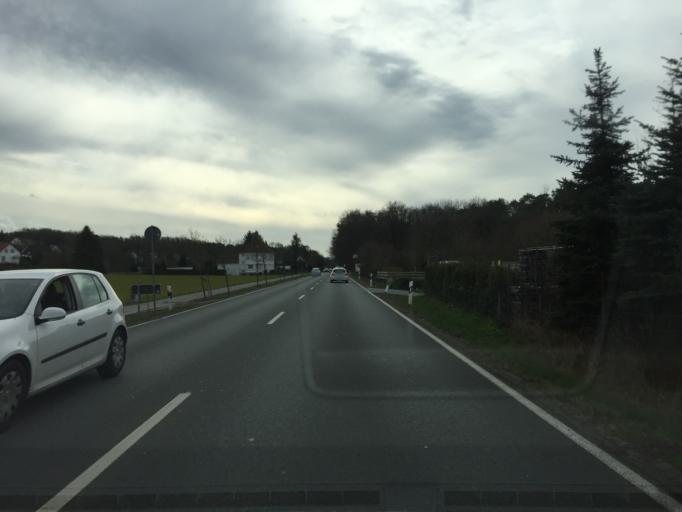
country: DE
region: North Rhine-Westphalia
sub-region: Regierungsbezirk Detmold
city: Lage
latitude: 52.0131
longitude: 8.7685
